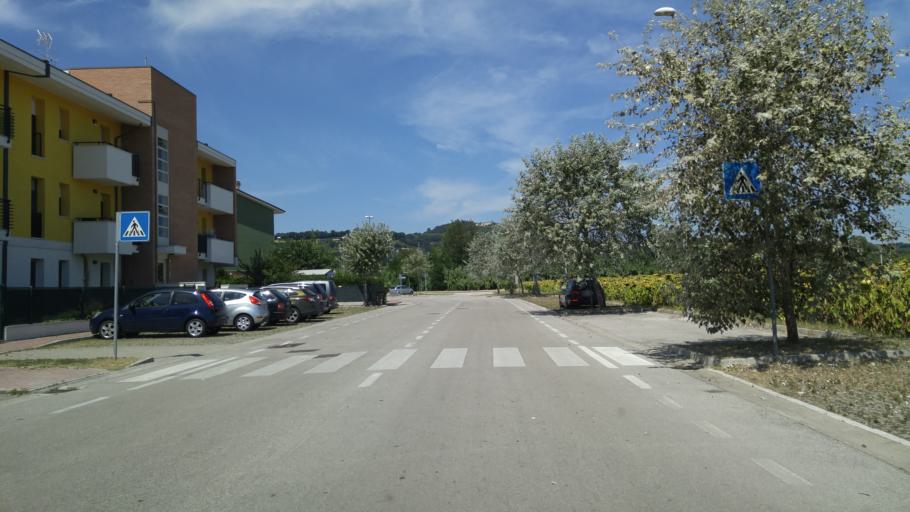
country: IT
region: The Marches
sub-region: Provincia di Pesaro e Urbino
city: Rosciano
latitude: 43.8048
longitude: 12.9940
